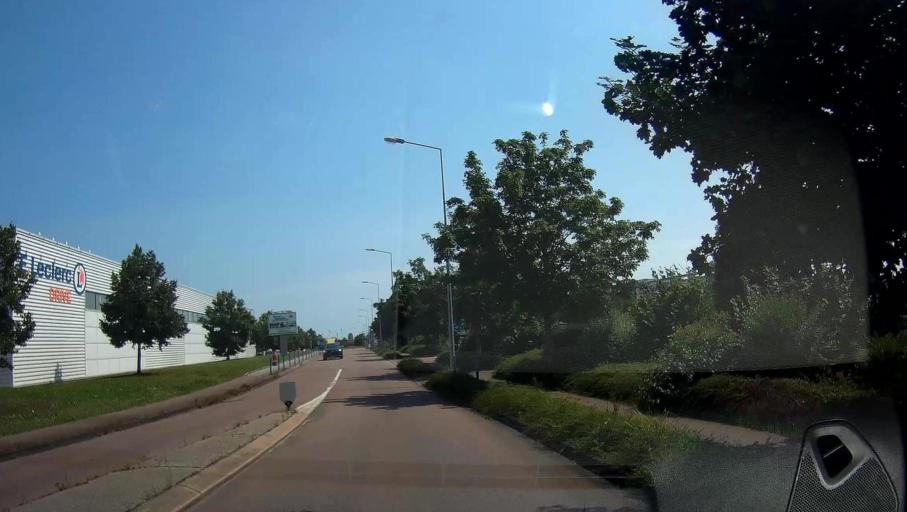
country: FR
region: Bourgogne
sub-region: Departement de la Cote-d'Or
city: Beaune
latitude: 47.0414
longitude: 4.8405
